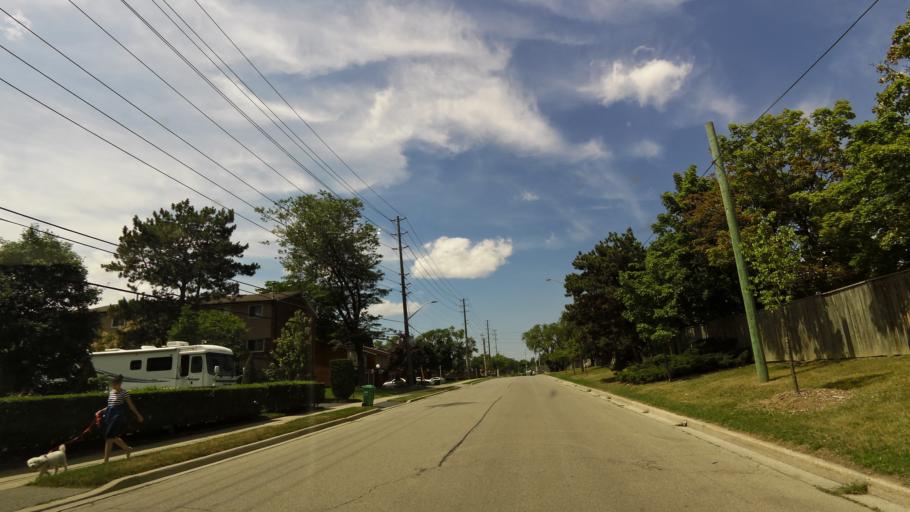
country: CA
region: Ontario
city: Etobicoke
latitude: 43.5911
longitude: -79.5712
